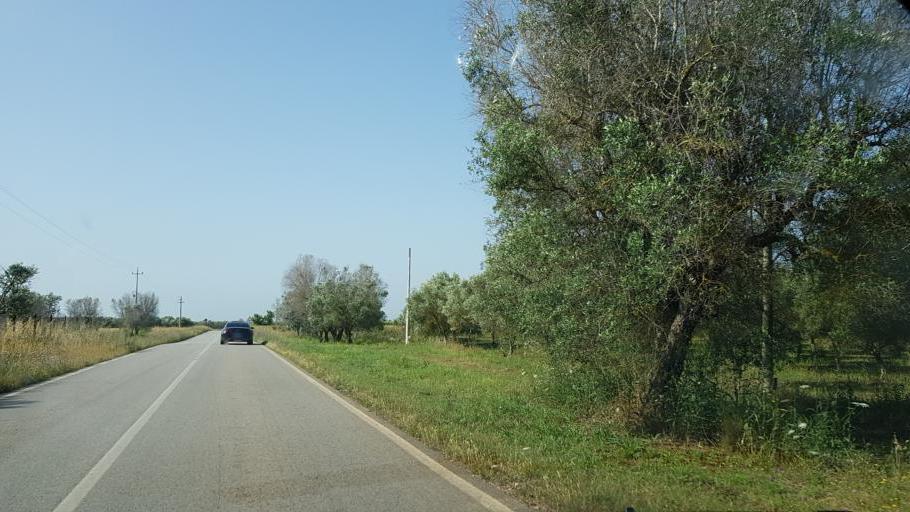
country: IT
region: Apulia
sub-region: Provincia di Brindisi
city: San Pancrazio Salentino
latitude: 40.4501
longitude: 17.8410
